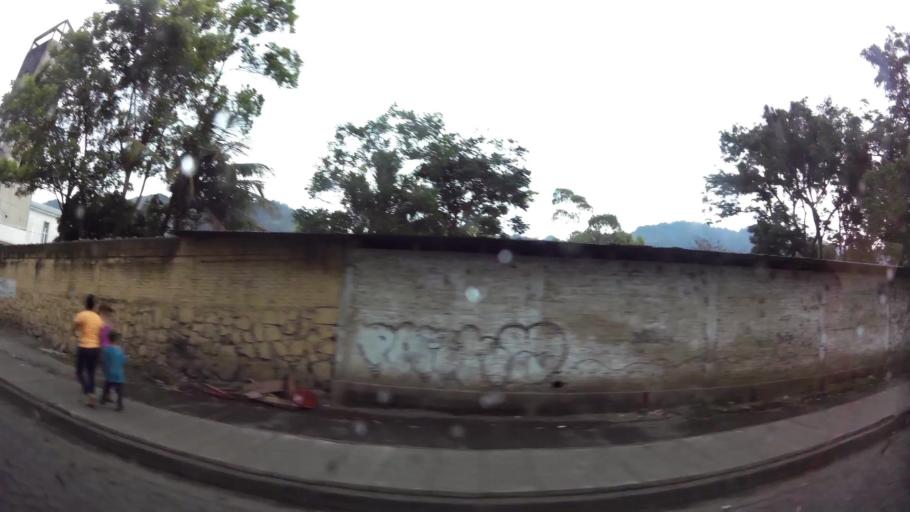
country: NI
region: Jinotega
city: Jinotega
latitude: 13.0893
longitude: -85.9992
